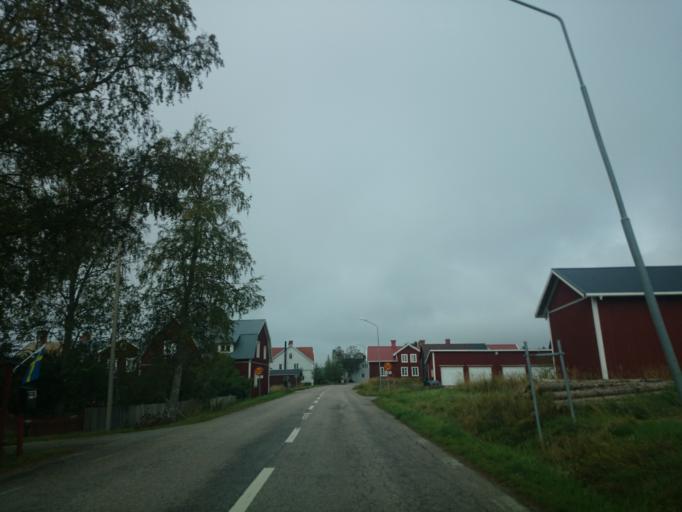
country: SE
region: Gaevleborg
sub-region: Nordanstigs Kommun
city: Bergsjoe
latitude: 61.9739
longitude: 17.2550
